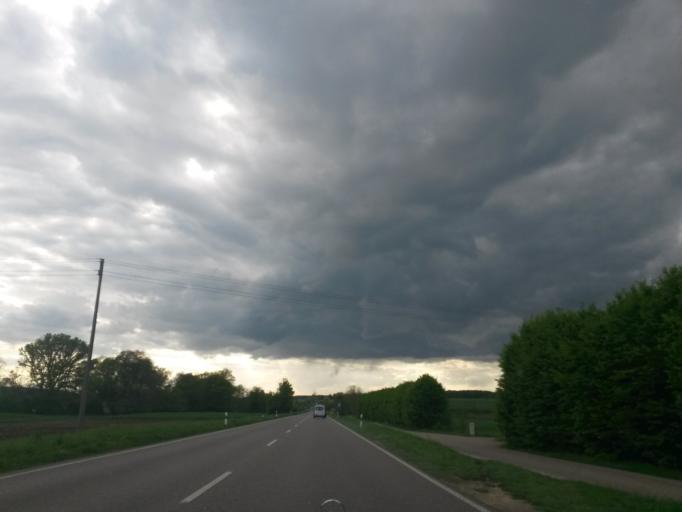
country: DE
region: Baden-Wuerttemberg
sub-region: Regierungsbezirk Stuttgart
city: Essingen
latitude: 48.8217
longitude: 10.0055
